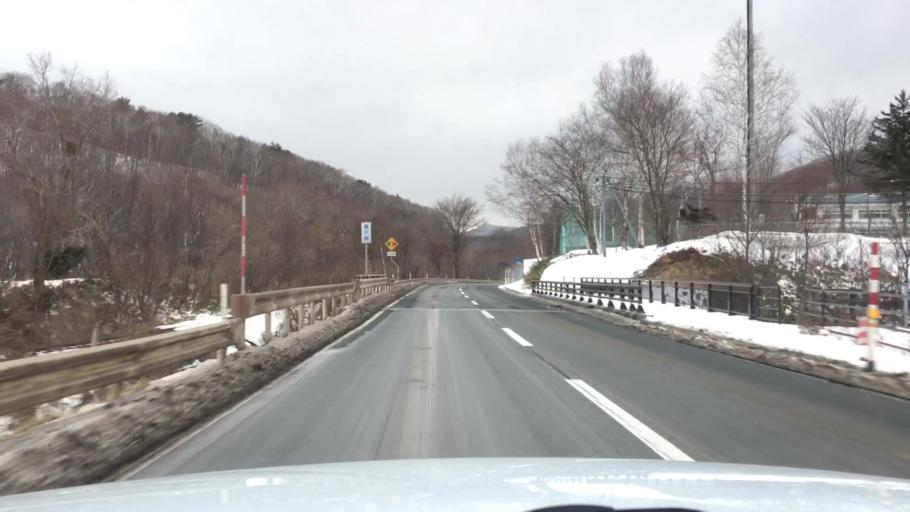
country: JP
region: Iwate
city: Morioka-shi
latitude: 39.6387
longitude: 141.4265
